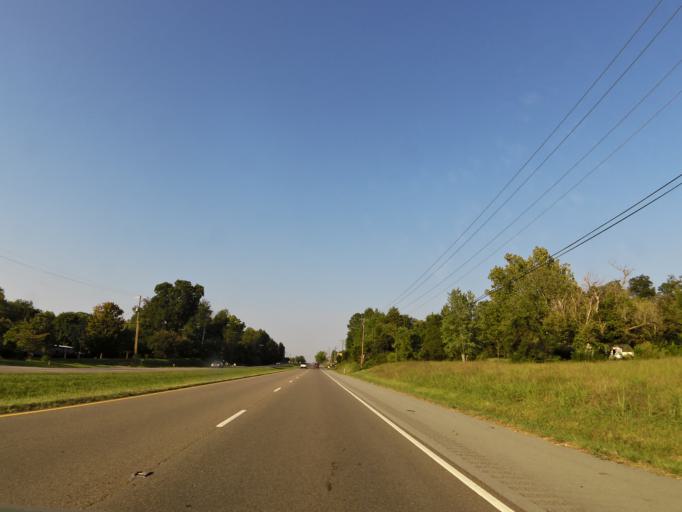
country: US
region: Tennessee
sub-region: Knox County
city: Mascot
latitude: 36.0349
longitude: -83.7247
